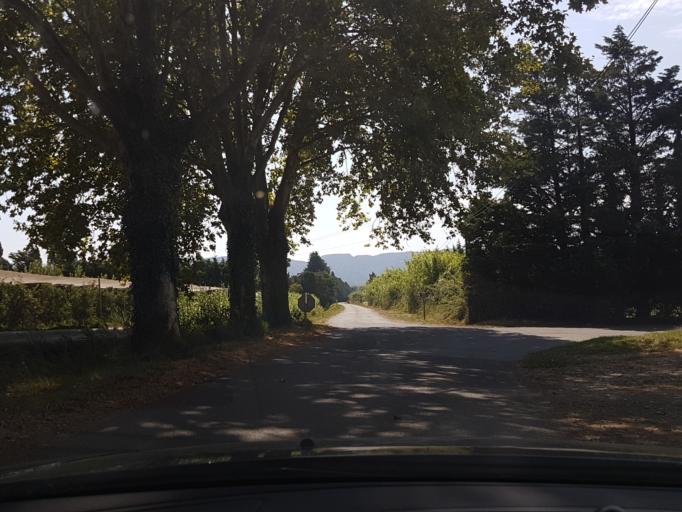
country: FR
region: Provence-Alpes-Cote d'Azur
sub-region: Departement des Bouches-du-Rhone
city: Saint-Remy-de-Provence
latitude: 43.8038
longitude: 4.8830
